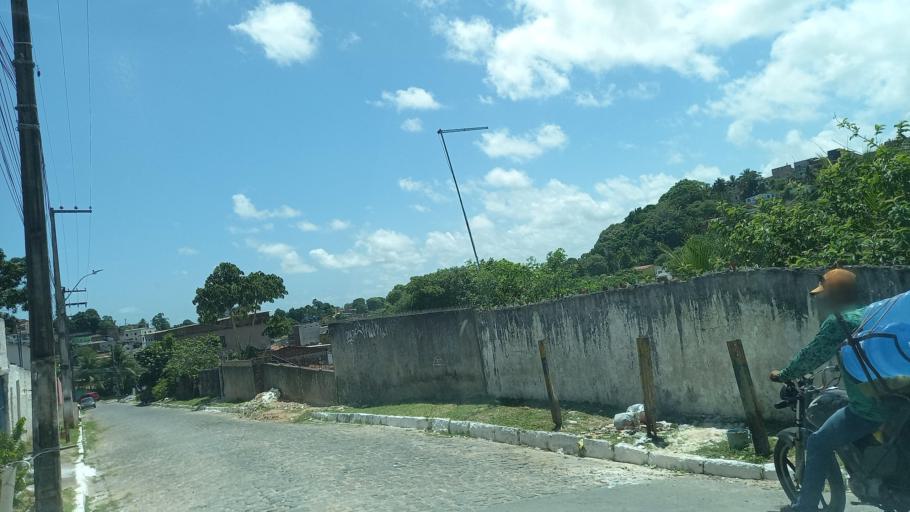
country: BR
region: Pernambuco
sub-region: Jaboatao Dos Guararapes
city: Jaboatao dos Guararapes
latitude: -8.1340
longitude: -34.9567
